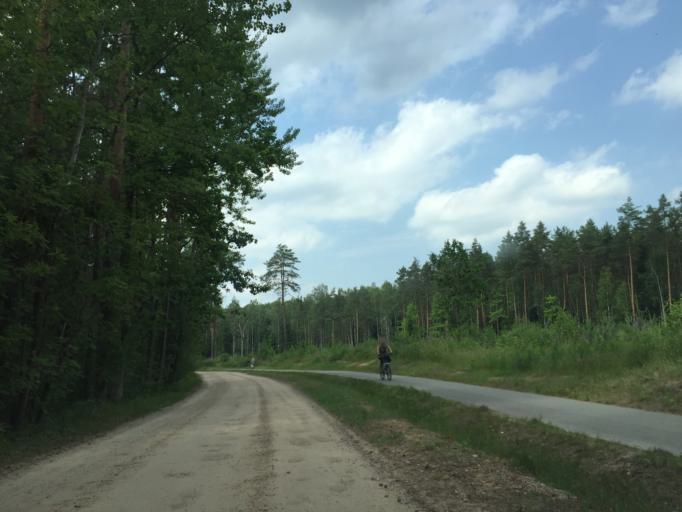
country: LV
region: Olaine
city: Olaine
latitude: 56.7792
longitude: 23.8876
